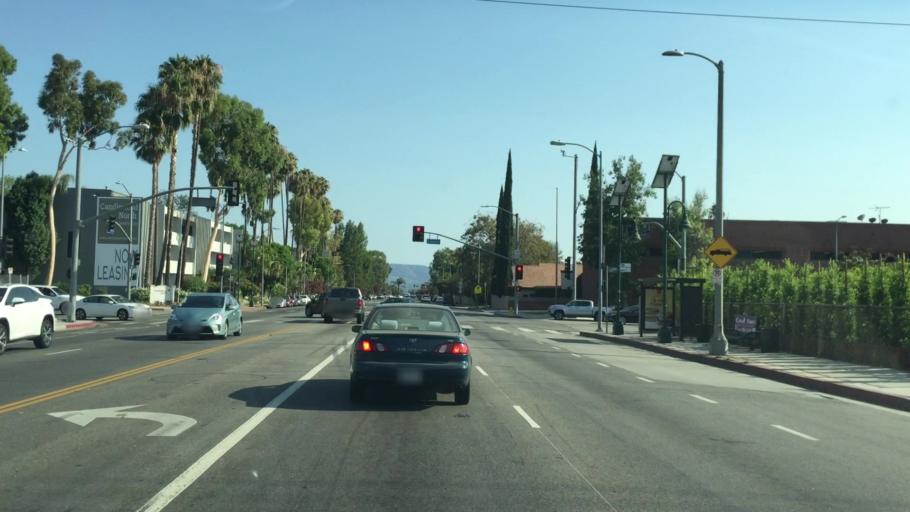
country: US
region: California
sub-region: Los Angeles County
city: Northridge
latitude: 34.2505
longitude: -118.5361
